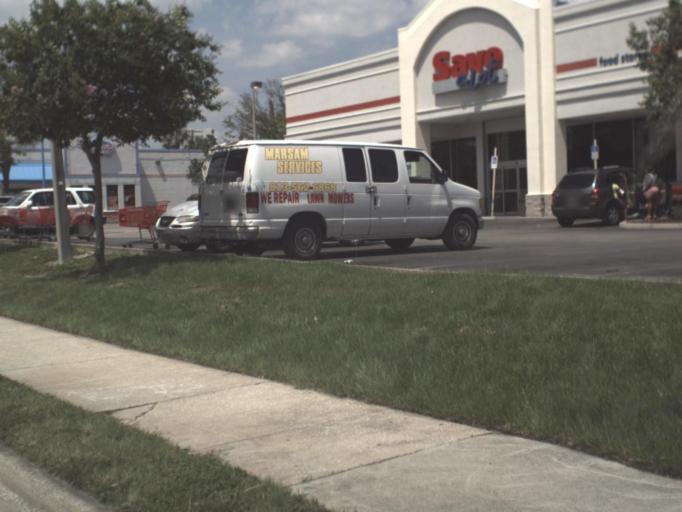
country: US
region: Florida
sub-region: Hillsborough County
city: East Lake-Orient Park
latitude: 27.9621
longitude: -82.4018
